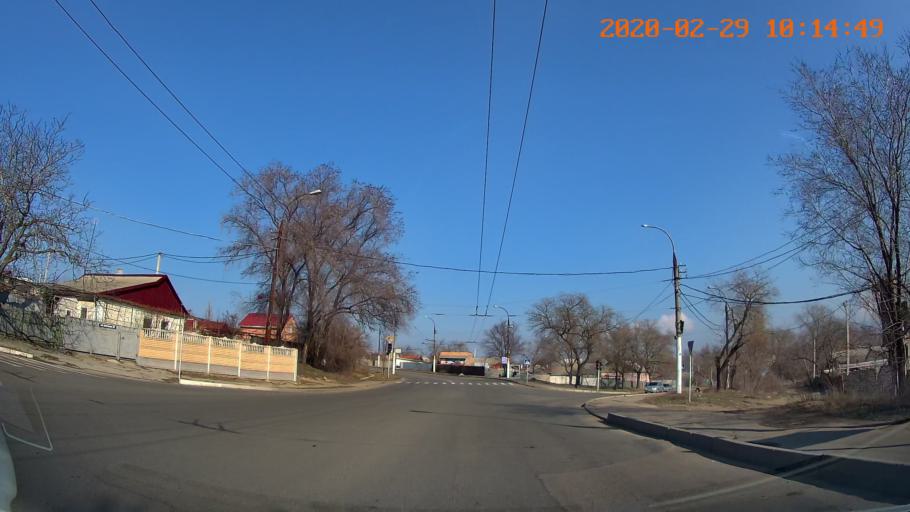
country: MD
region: Telenesti
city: Tiraspolul Nou
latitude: 46.8505
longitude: 29.6432
